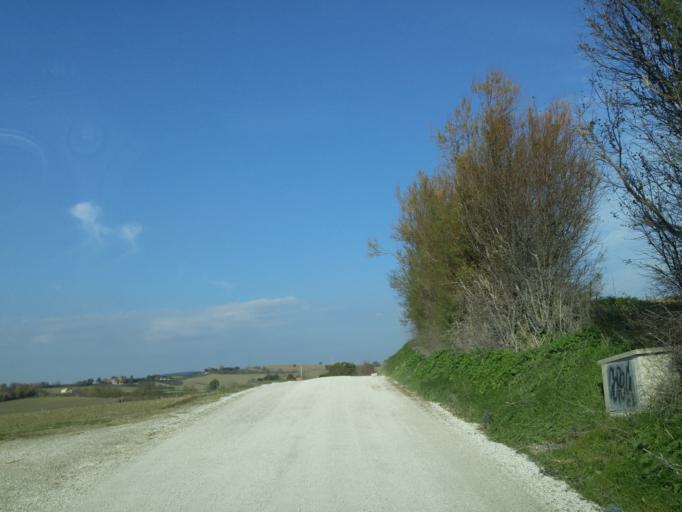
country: IT
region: The Marches
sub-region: Provincia di Pesaro e Urbino
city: Lucrezia
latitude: 43.7930
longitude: 12.9249
